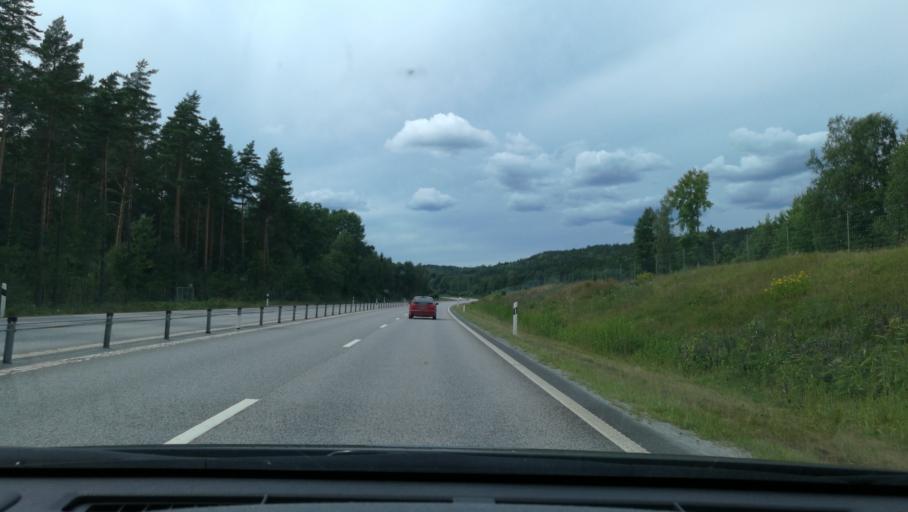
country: SE
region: OEstergoetland
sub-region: Norrkopings Kommun
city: Svartinge
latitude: 58.6404
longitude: 16.0909
